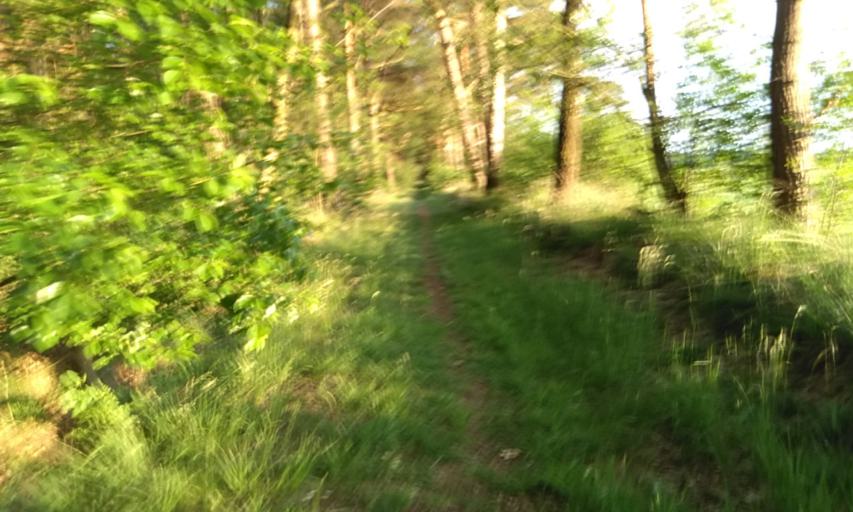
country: DE
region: Lower Saxony
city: Agathenburg
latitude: 53.5286
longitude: 9.4985
